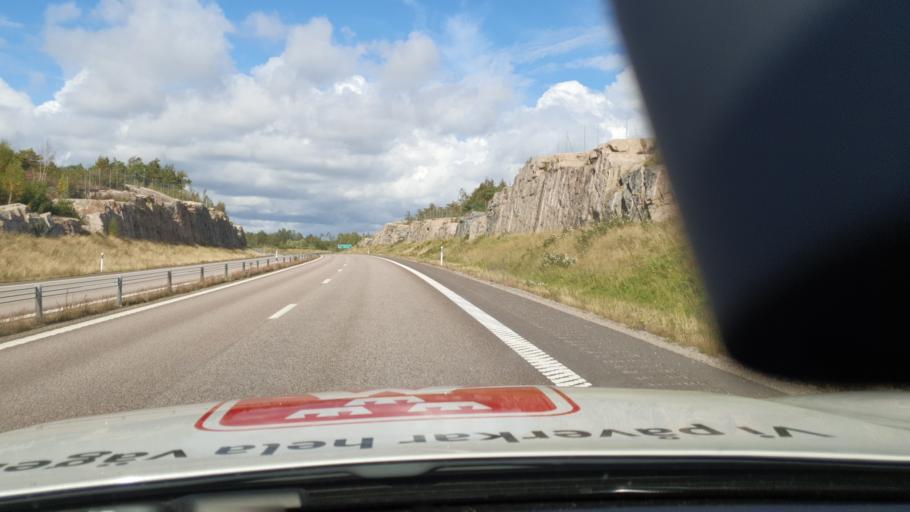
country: SE
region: Vaestra Goetaland
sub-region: Tanums Kommun
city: Tanumshede
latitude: 58.8421
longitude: 11.2810
